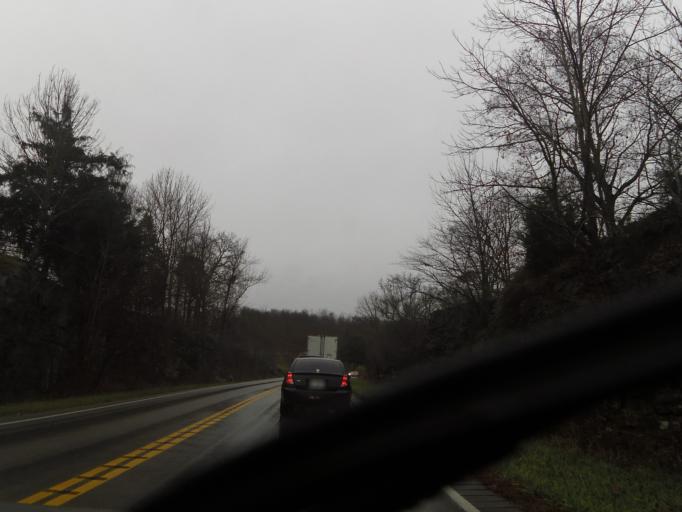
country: US
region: Kentucky
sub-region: Rockcastle County
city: Mount Vernon
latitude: 37.4168
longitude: -84.3334
